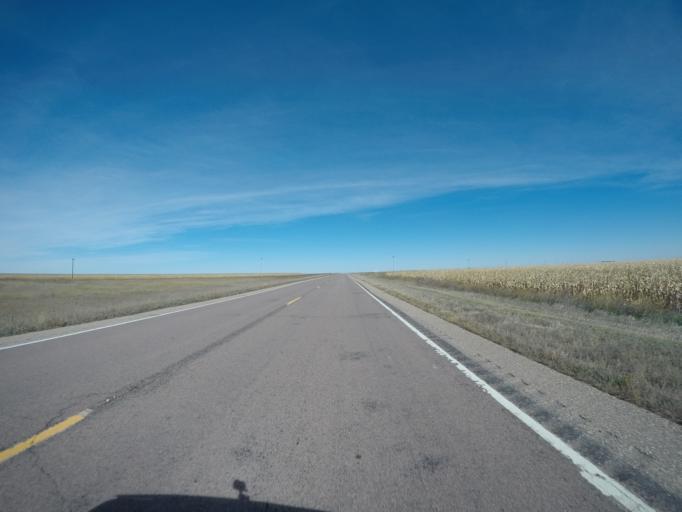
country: US
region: Colorado
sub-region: Kit Carson County
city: Burlington
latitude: 39.6708
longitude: -102.4213
